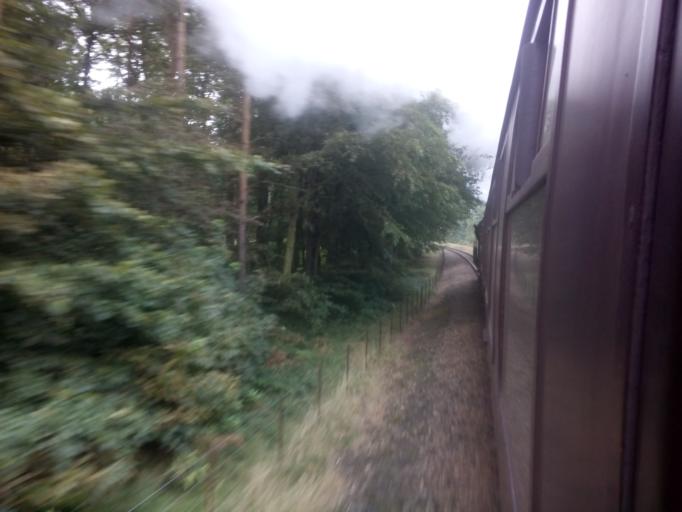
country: GB
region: England
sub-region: Norfolk
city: Briston
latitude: 52.9257
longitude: 1.1169
